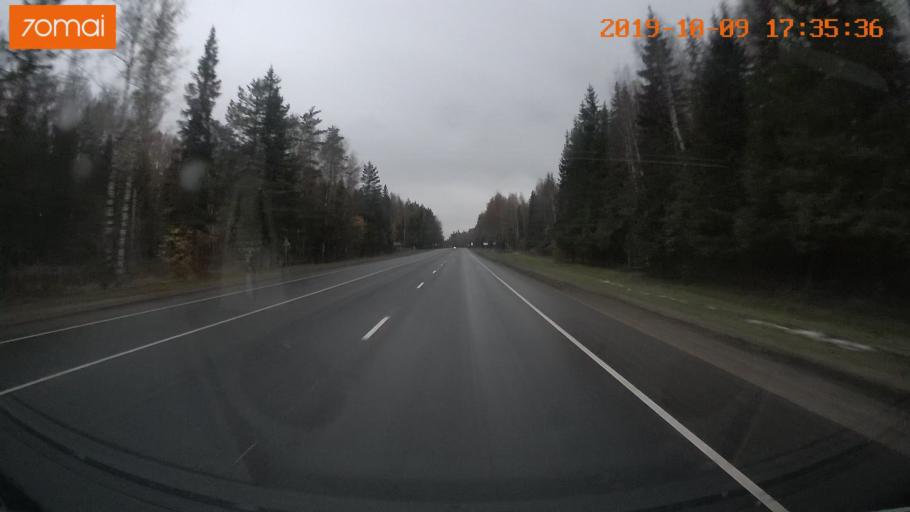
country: RU
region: Ivanovo
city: Bogorodskoye
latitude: 57.0909
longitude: 41.0010
